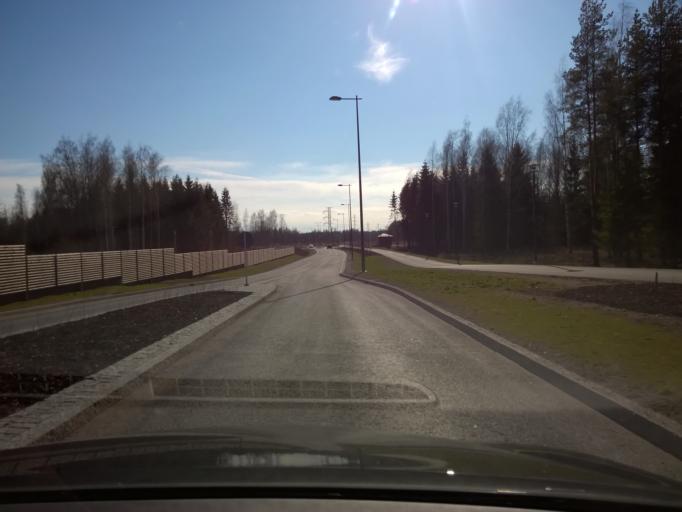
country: FI
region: Uusimaa
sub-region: Helsinki
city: Kilo
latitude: 60.1882
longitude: 24.7796
